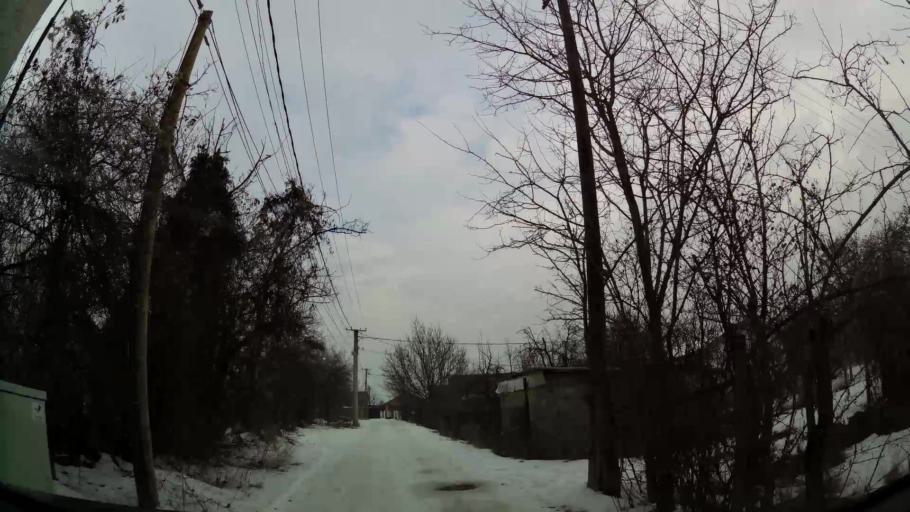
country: MK
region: Saraj
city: Saraj
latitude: 42.0381
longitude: 21.3597
